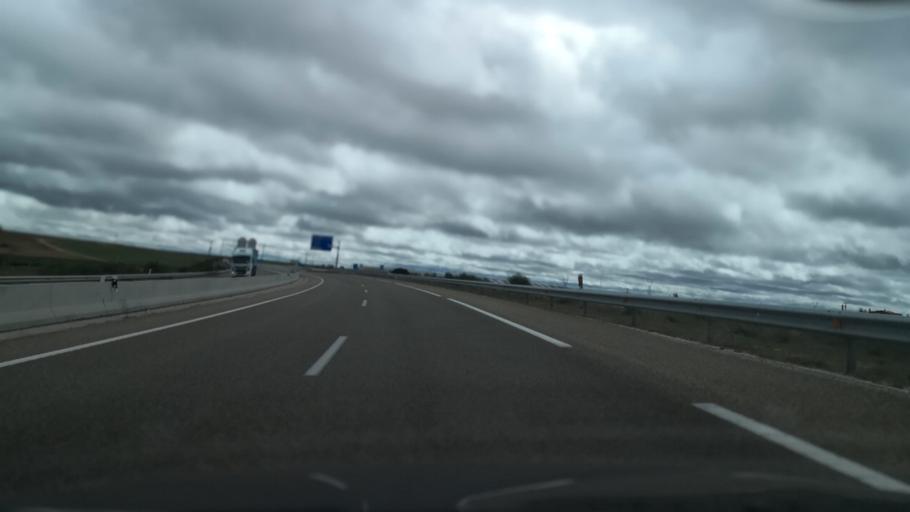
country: ES
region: Castille and Leon
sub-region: Provincia de Zamora
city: Valcabado
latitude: 41.5503
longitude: -5.7573
